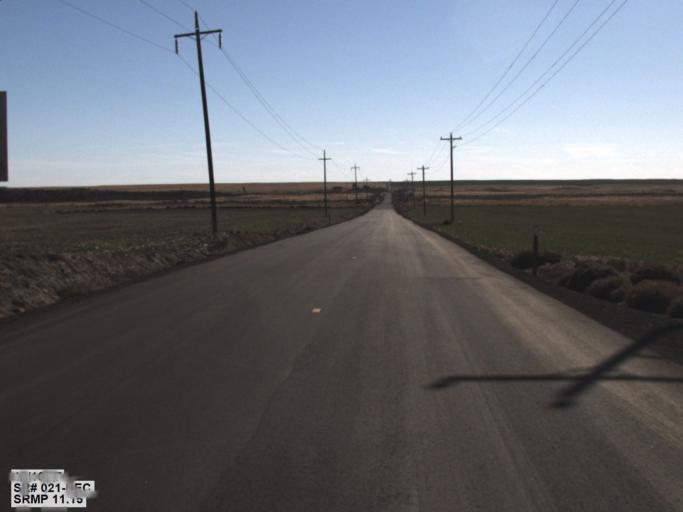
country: US
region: Washington
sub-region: Franklin County
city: Connell
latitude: 46.7877
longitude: -118.5473
